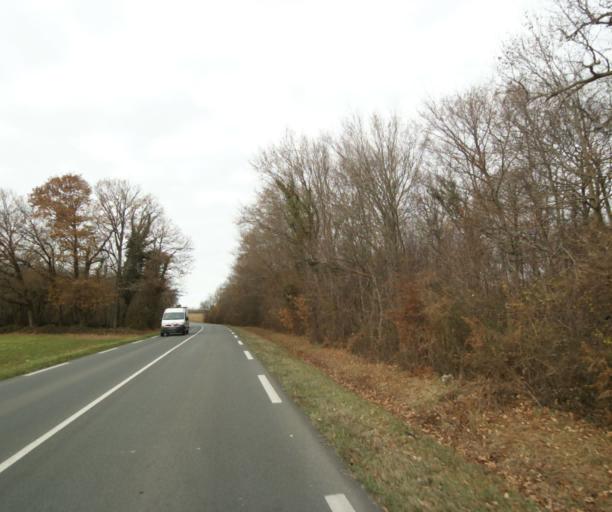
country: FR
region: Poitou-Charentes
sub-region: Departement de la Charente-Maritime
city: Corme-Royal
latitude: 45.7364
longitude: -0.7800
